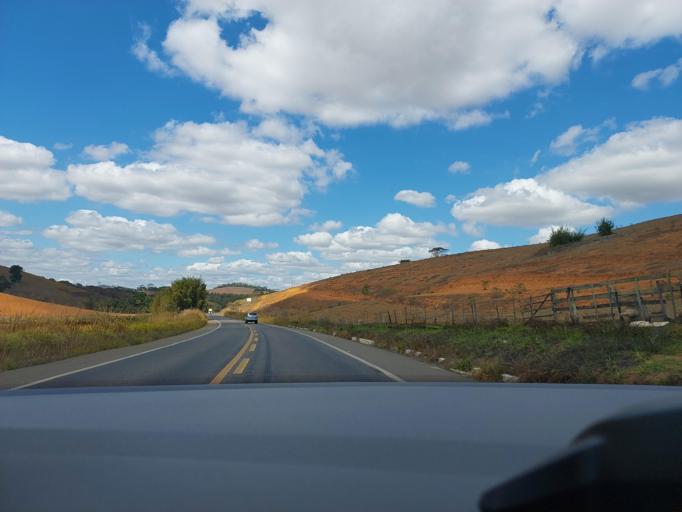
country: BR
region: Minas Gerais
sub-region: Muriae
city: Muriae
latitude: -21.1400
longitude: -42.1734
